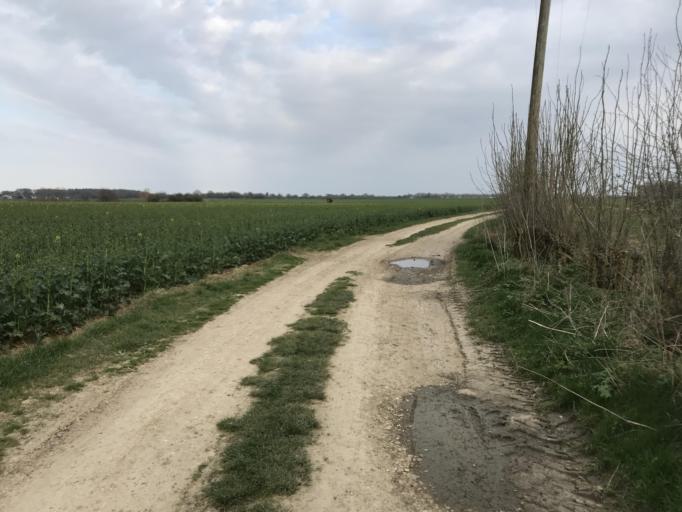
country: FR
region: Ile-de-France
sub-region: Departement de l'Essonne
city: Les Molieres
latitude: 48.6596
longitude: 2.0517
